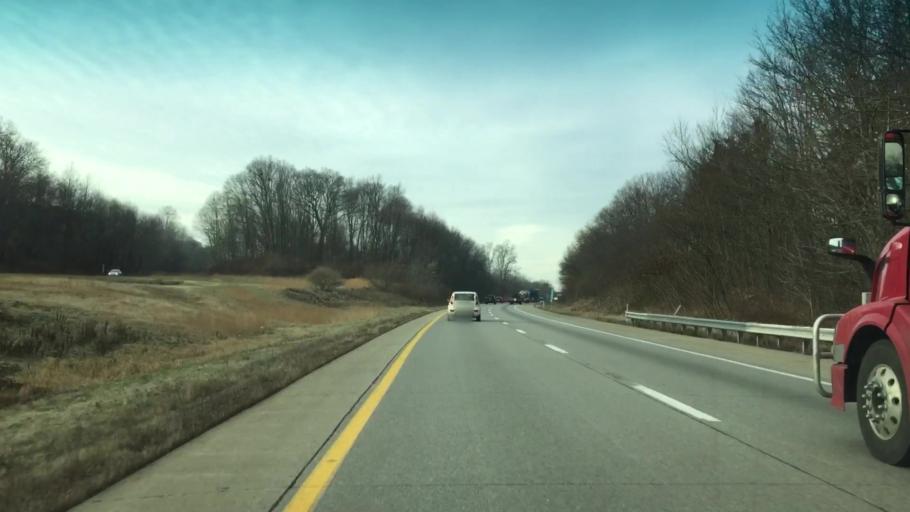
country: US
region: Pennsylvania
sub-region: Luzerne County
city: Nescopeck
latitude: 41.0170
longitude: -76.1986
